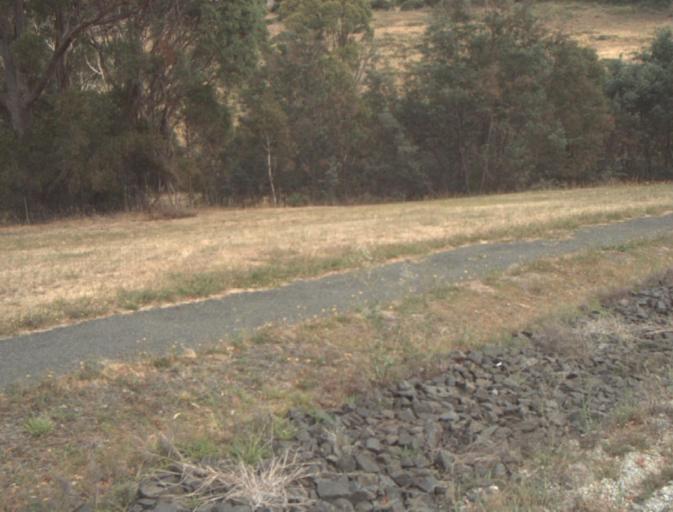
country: AU
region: Tasmania
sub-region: Launceston
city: Newstead
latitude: -41.4761
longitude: 147.1814
